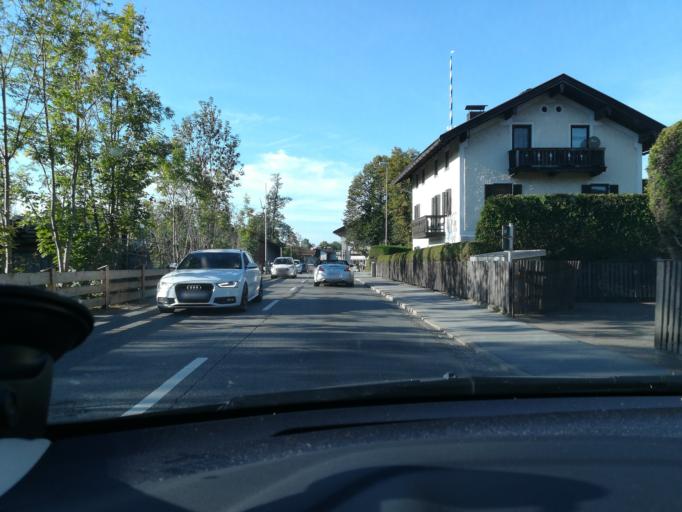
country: DE
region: Bavaria
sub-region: Upper Bavaria
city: Hausham
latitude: 47.7654
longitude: 11.8258
